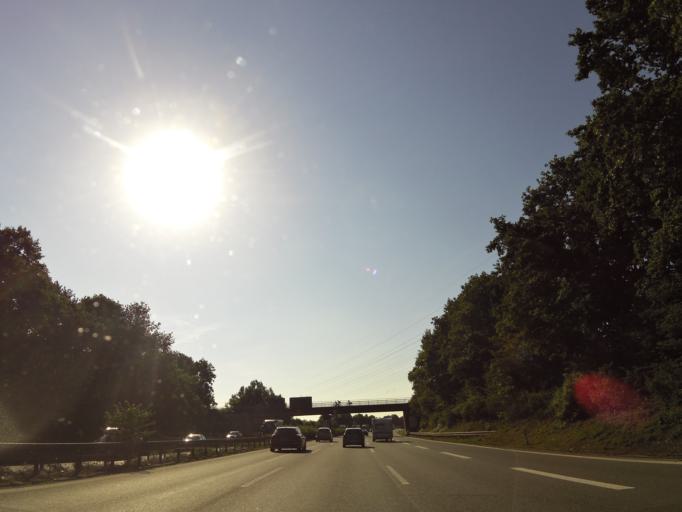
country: DE
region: Bavaria
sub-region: Regierungsbezirk Mittelfranken
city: Erlangen
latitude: 49.5588
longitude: 10.9970
